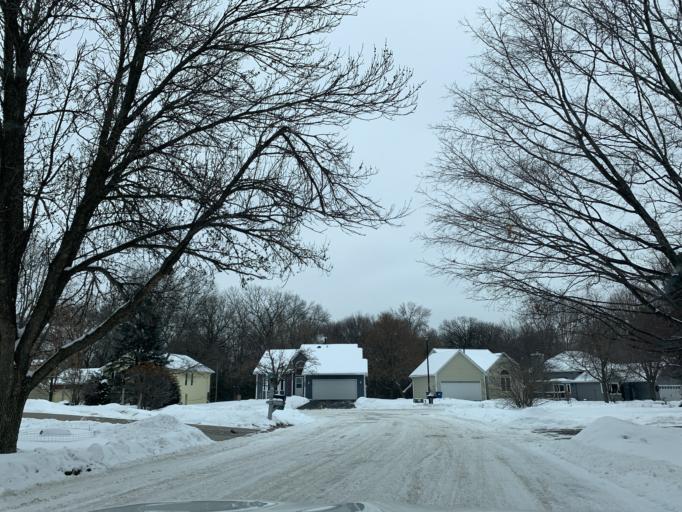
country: US
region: Minnesota
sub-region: Anoka County
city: Coon Rapids
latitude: 45.1590
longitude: -93.2996
